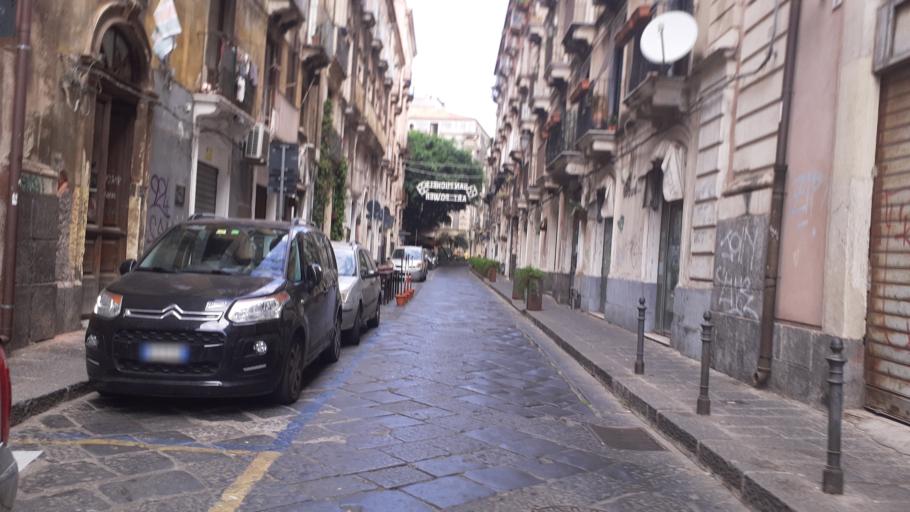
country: IT
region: Sicily
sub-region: Catania
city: Catania
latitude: 37.5057
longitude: 15.0877
